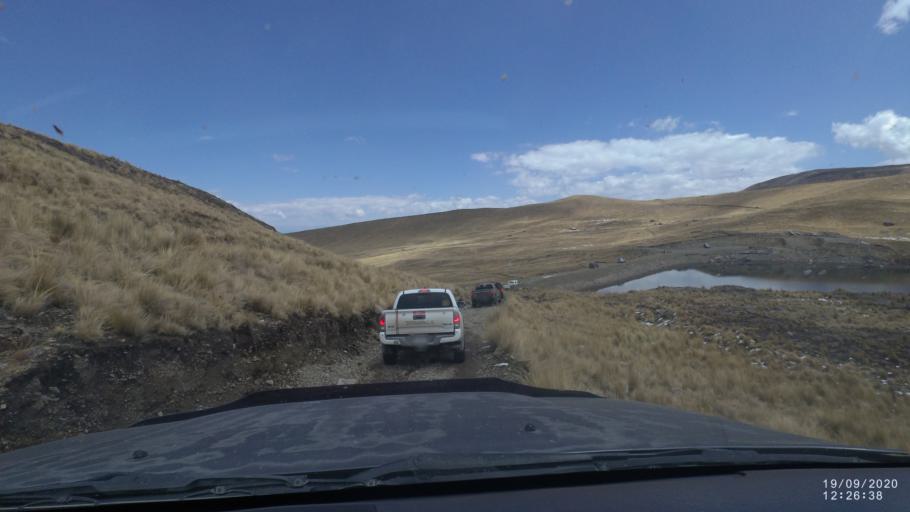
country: BO
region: Cochabamba
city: Cochabamba
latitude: -17.2943
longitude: -66.1118
